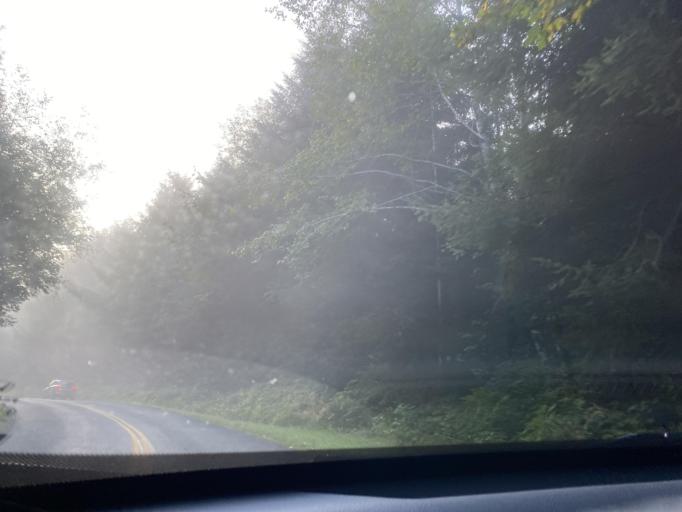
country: US
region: Washington
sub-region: Clallam County
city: Forks
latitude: 47.8083
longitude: -124.0945
